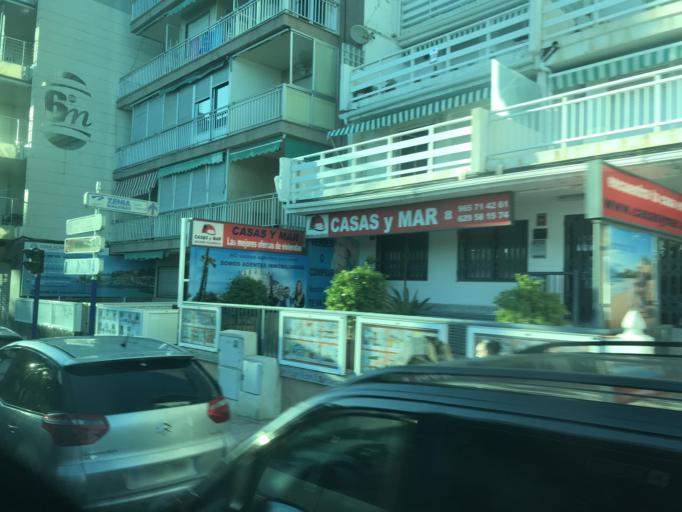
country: ES
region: Valencia
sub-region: Provincia de Alicante
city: Torrevieja
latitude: 37.9807
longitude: -0.6642
